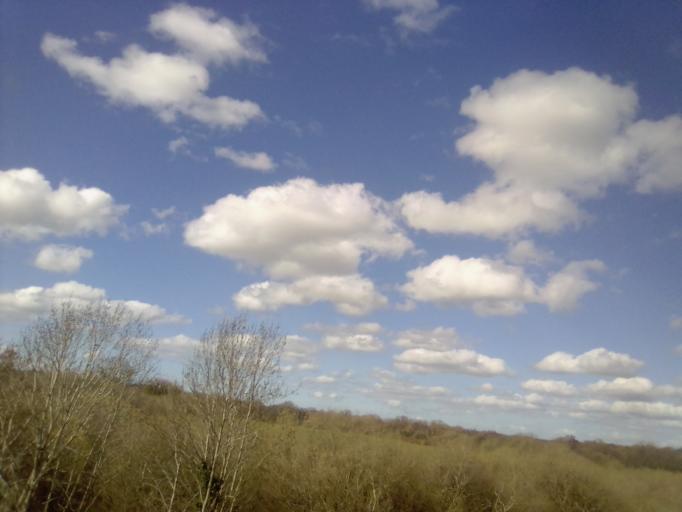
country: IE
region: Munster
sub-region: County Cork
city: Kanturk
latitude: 52.1255
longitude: -8.9106
